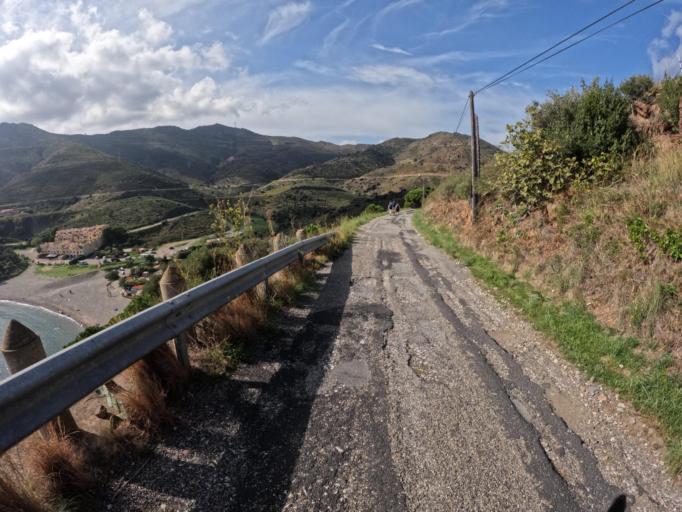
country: FR
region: Languedoc-Roussillon
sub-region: Departement des Pyrenees-Orientales
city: Cervera de la Marenda
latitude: 42.4616
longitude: 3.1575
